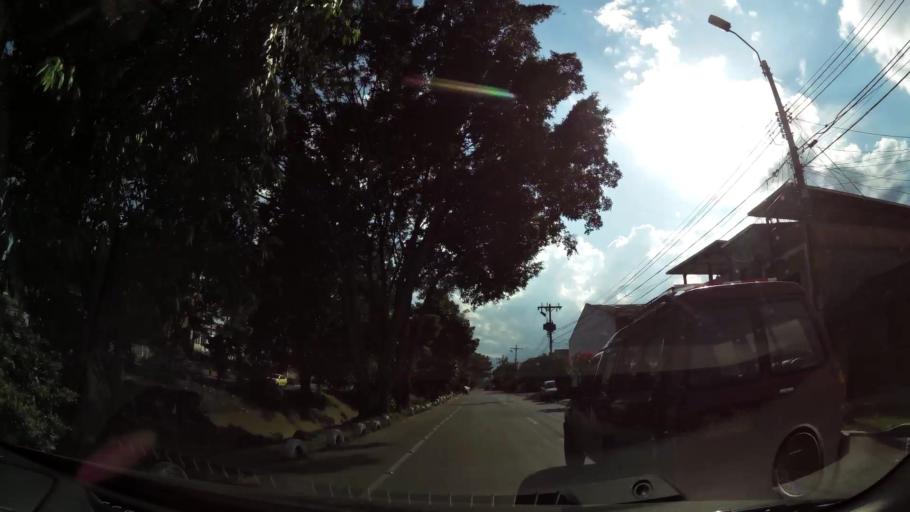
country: CO
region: Valle del Cauca
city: Cali
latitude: 3.4074
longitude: -76.5051
